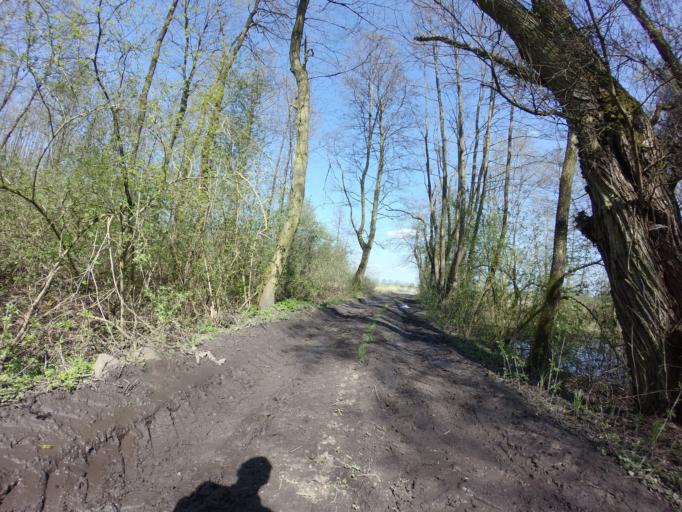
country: PL
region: West Pomeranian Voivodeship
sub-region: Powiat choszczenski
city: Choszczno
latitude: 53.1651
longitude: 15.4667
